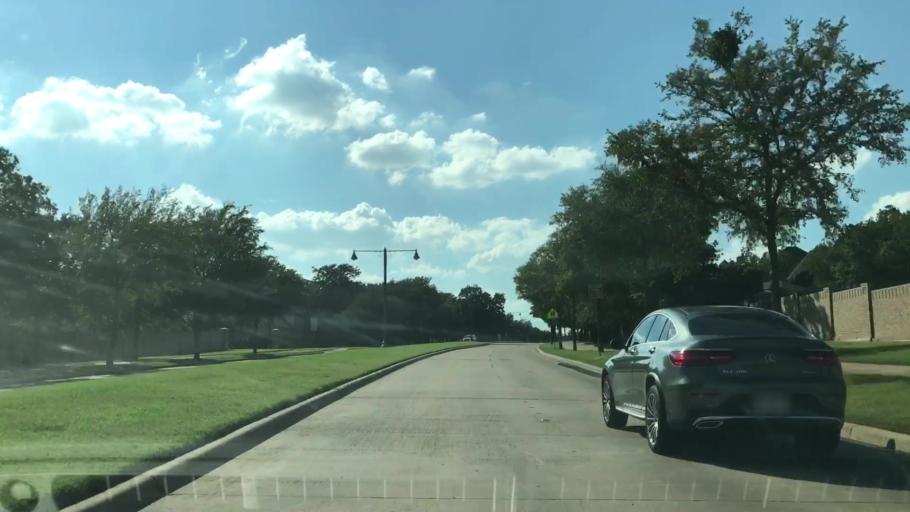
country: US
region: Texas
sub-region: Tarrant County
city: Keller
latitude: 32.9205
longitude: -97.2089
